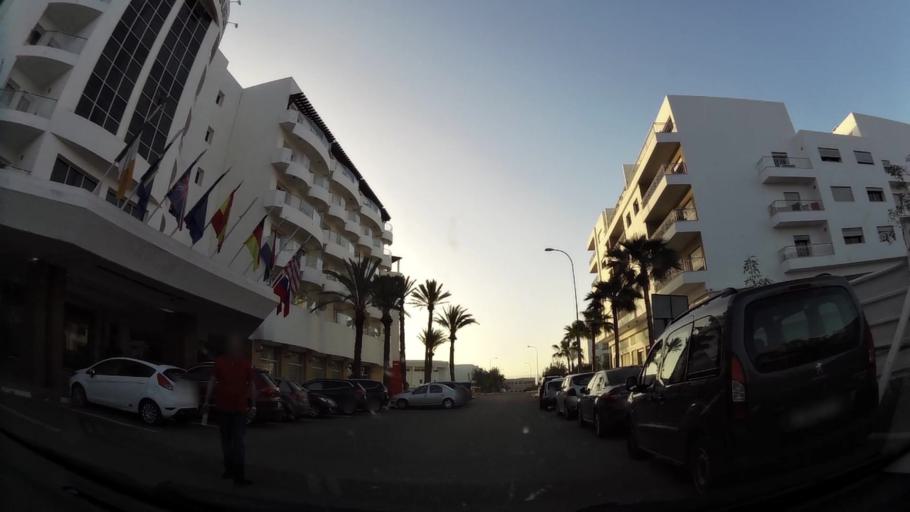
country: MA
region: Souss-Massa-Draa
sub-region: Agadir-Ida-ou-Tnan
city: Agadir
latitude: 30.4005
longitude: -9.5910
